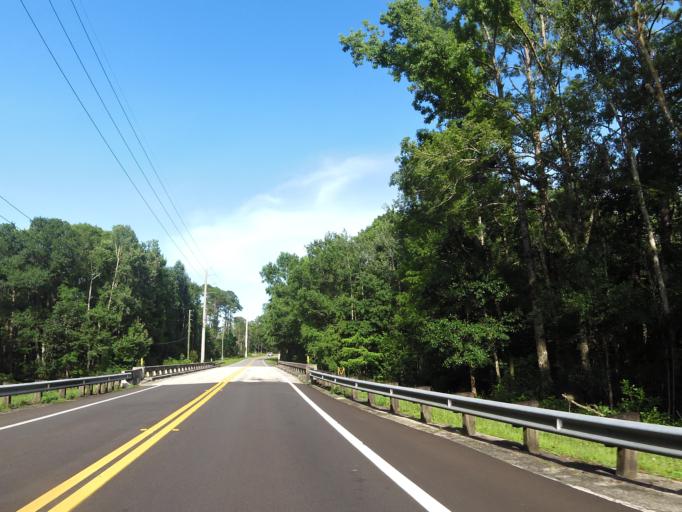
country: US
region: Florida
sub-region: Clay County
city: Green Cove Springs
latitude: 30.0149
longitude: -81.5644
